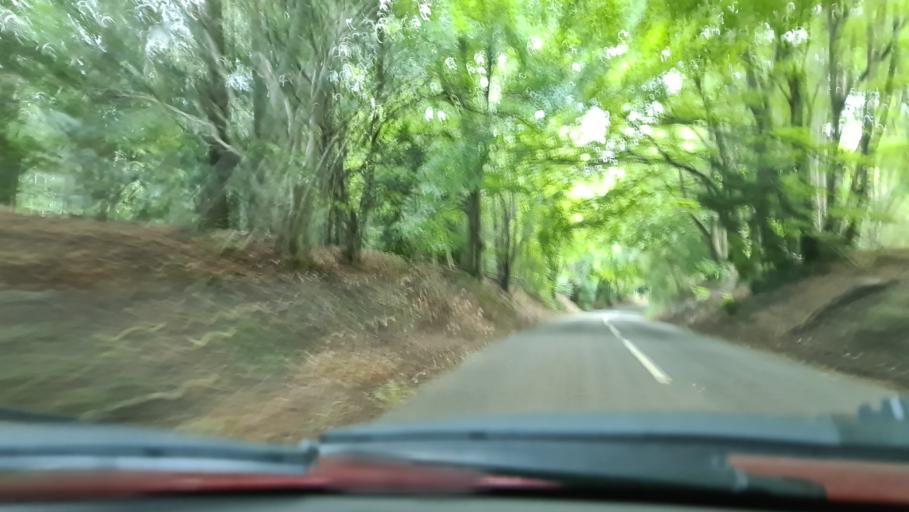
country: GB
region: England
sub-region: Buckinghamshire
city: Princes Risborough
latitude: 51.7329
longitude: -0.8015
